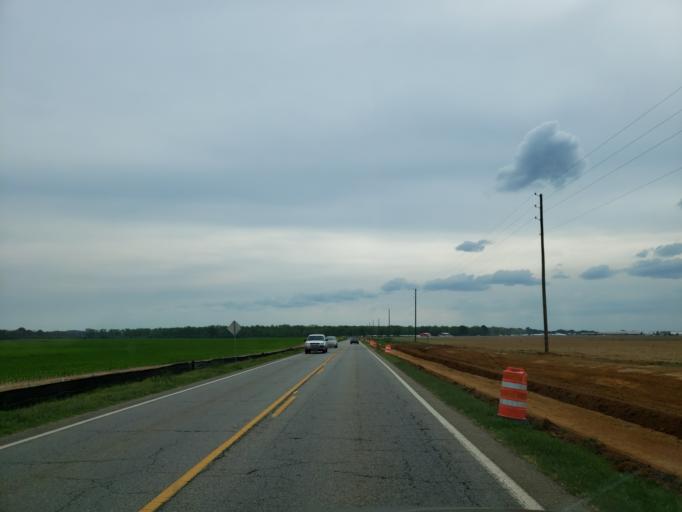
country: US
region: Georgia
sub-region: Macon County
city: Montezuma
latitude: 32.3620
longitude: -83.9574
